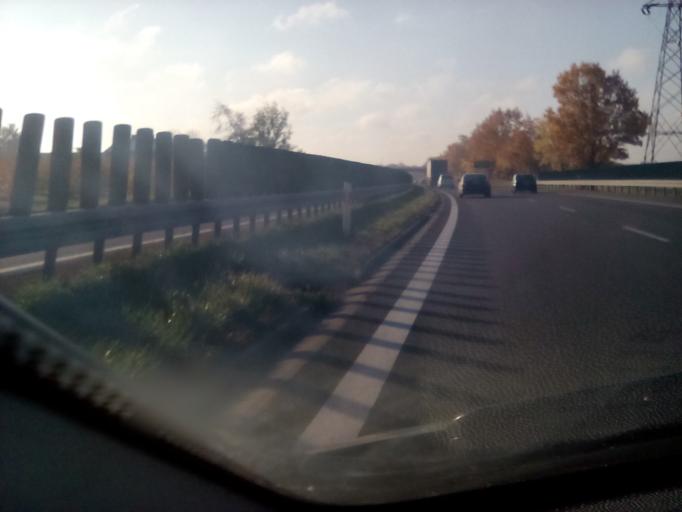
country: PL
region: Masovian Voivodeship
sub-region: Powiat grojecki
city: Grojec
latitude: 51.8895
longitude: 20.8562
